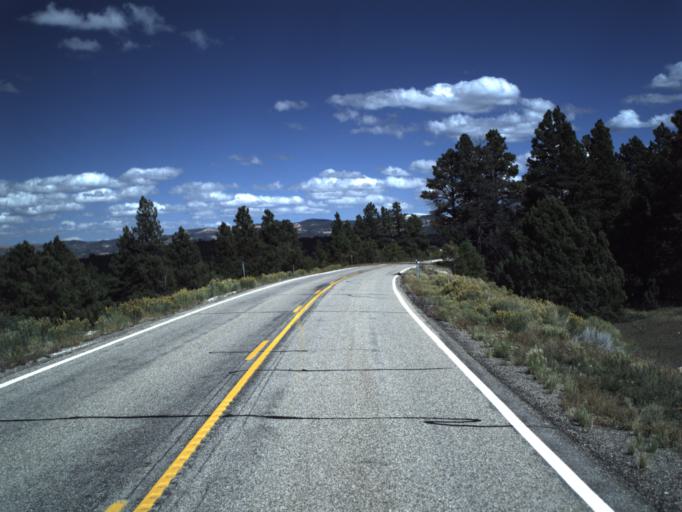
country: US
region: Utah
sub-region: Garfield County
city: Panguitch
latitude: 37.4966
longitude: -112.5485
